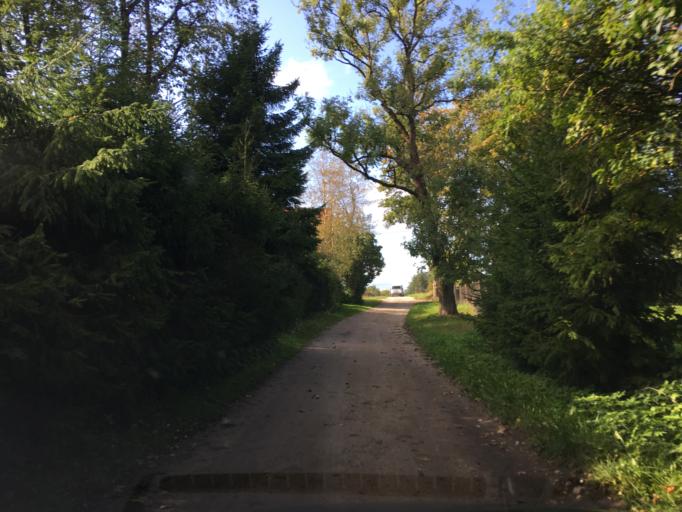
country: EE
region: Harju
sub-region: Saku vald
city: Saku
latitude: 59.3355
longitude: 24.6541
